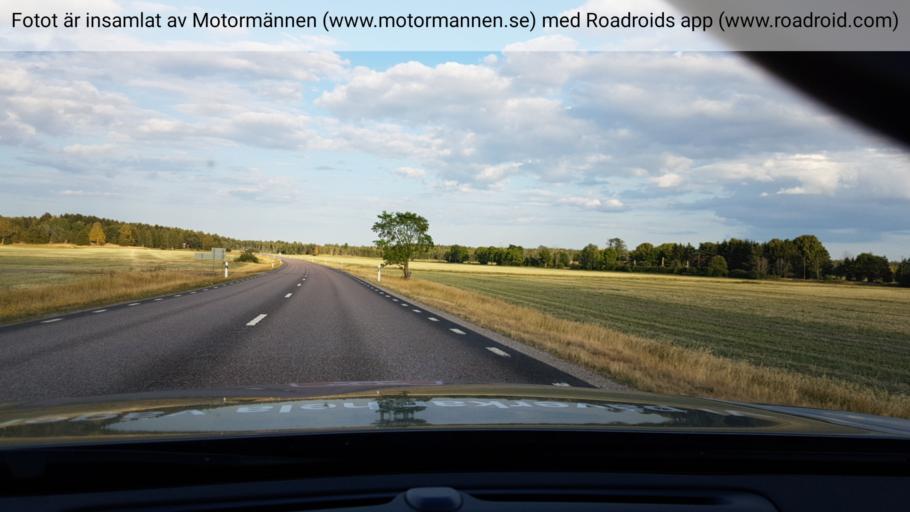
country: SE
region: Uppsala
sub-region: Enkopings Kommun
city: Orsundsbro
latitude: 59.8741
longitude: 17.2947
